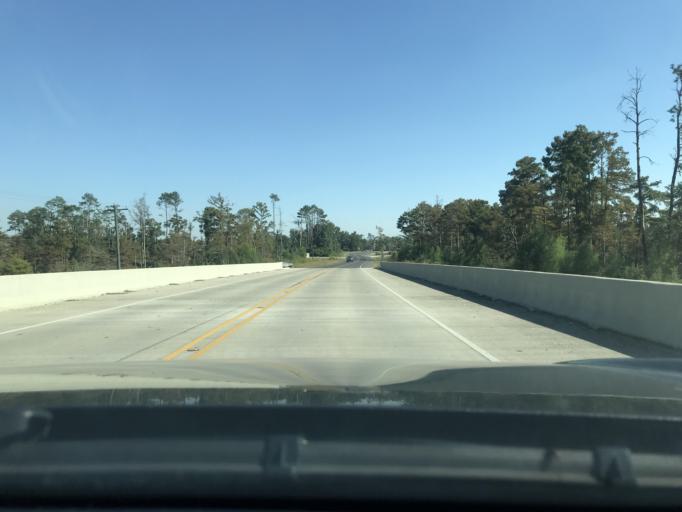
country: US
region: Louisiana
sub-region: Calcasieu Parish
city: Moss Bluff
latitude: 30.3031
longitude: -93.2476
